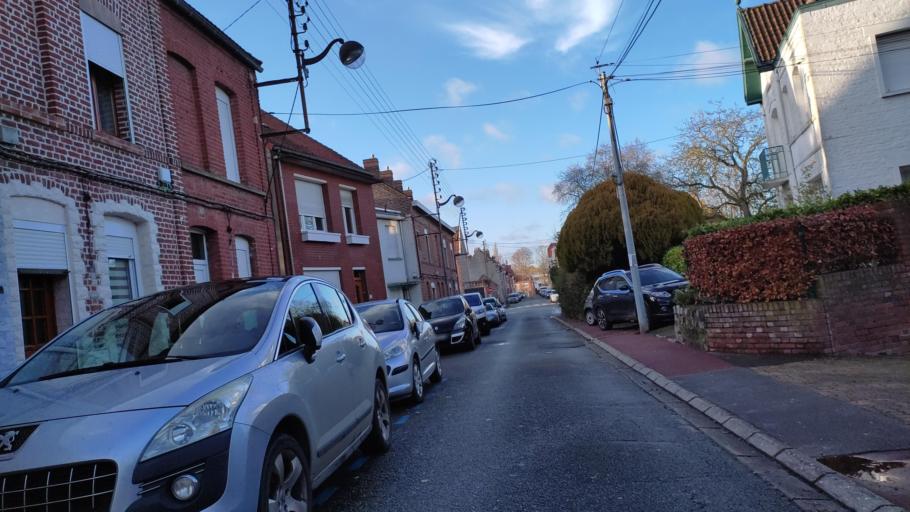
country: FR
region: Nord-Pas-de-Calais
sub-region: Departement du Pas-de-Calais
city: Bethune
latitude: 50.5280
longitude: 2.6480
